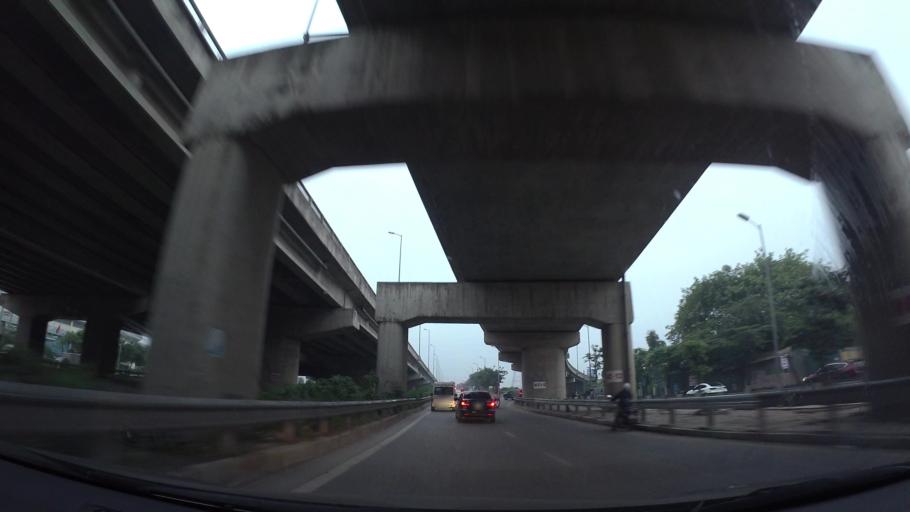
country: VN
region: Ha Noi
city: Van Dien
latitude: 20.9655
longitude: 105.8454
